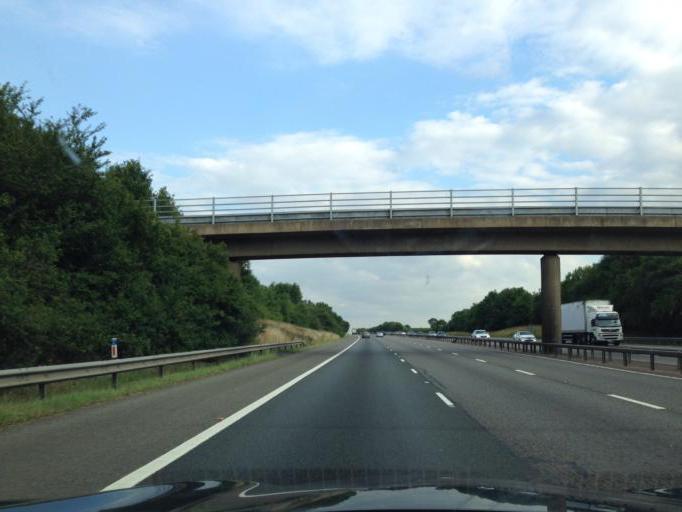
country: GB
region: England
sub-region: Warwickshire
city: Harbury
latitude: 52.1567
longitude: -1.4261
